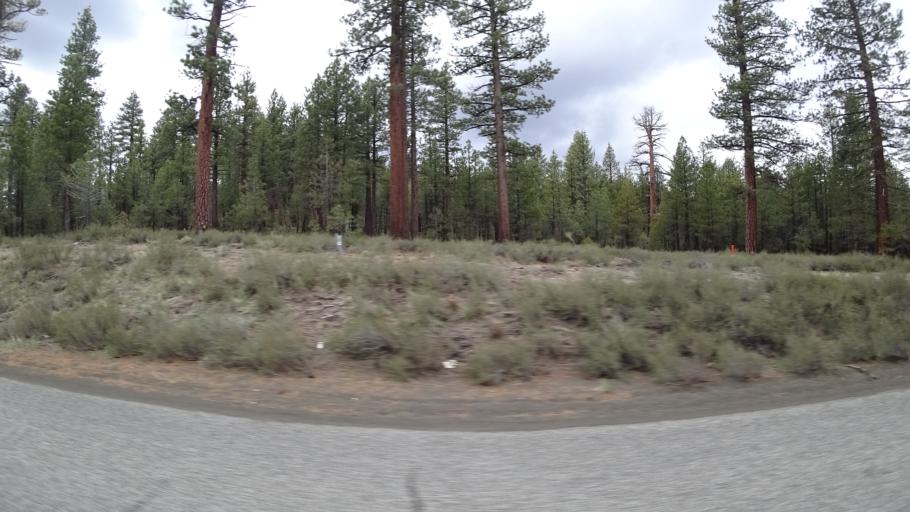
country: US
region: California
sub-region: Mono County
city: Mammoth Lakes
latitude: 37.7162
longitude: -118.9569
